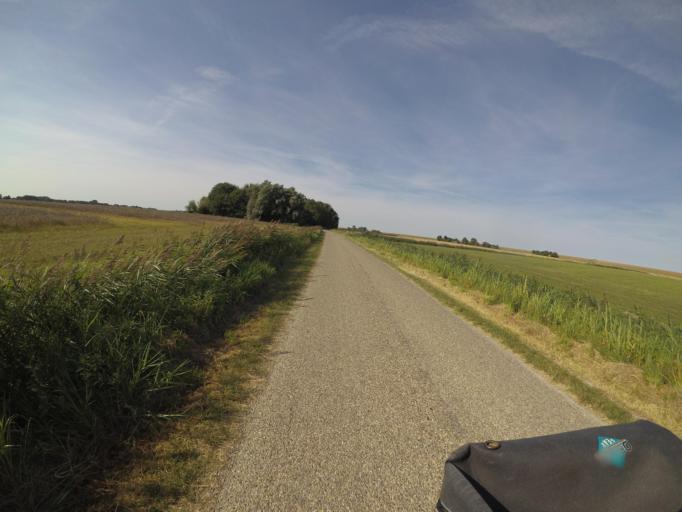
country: NL
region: Friesland
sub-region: Gemeente Ferwerderadiel
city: Marrum
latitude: 53.3415
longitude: 5.8056
